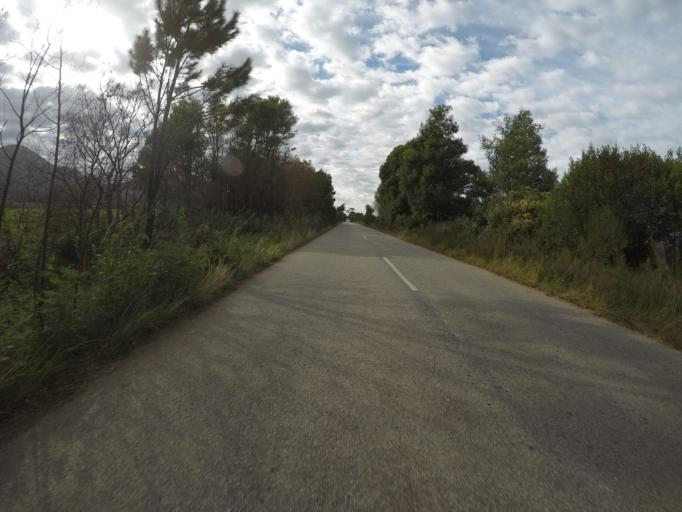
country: ZA
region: Eastern Cape
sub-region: Cacadu District Municipality
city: Kareedouw
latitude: -34.0435
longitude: 24.4264
